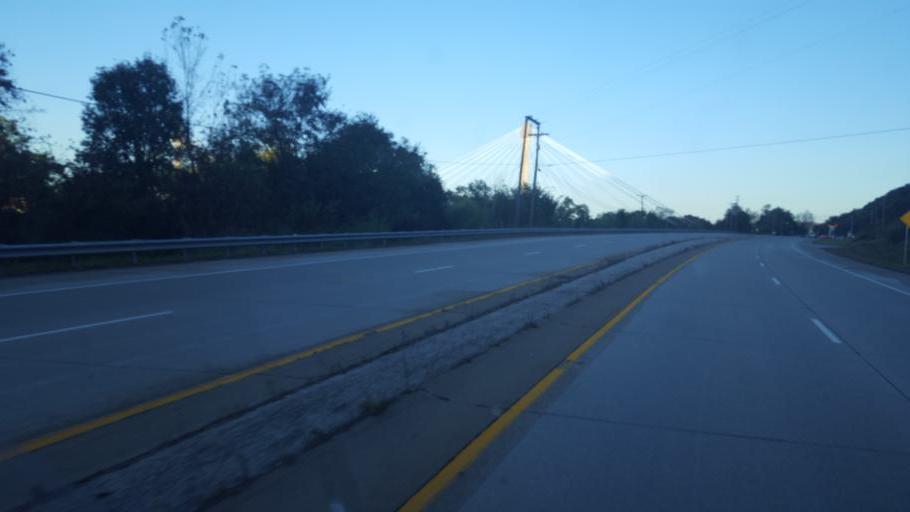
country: US
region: Ohio
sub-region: Scioto County
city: Portsmouth
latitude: 38.7256
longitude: -83.0022
